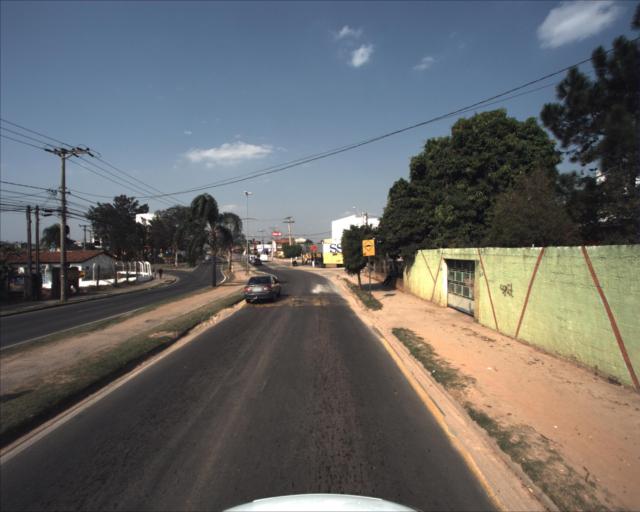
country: BR
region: Sao Paulo
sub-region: Sorocaba
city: Sorocaba
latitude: -23.4369
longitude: -47.4706
